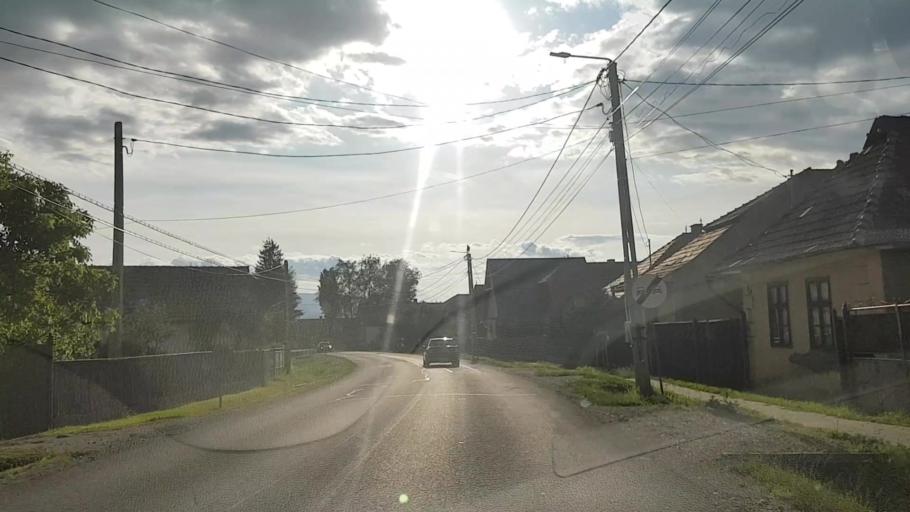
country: RO
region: Harghita
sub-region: Comuna Joseni
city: Joseni
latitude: 46.7025
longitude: 25.5121
